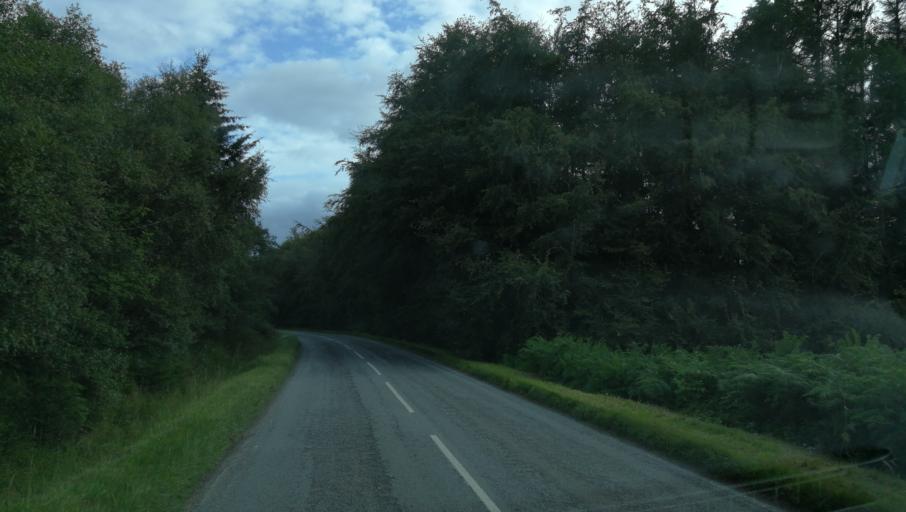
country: GB
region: Scotland
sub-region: Highland
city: Alness
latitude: 58.0374
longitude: -4.4245
